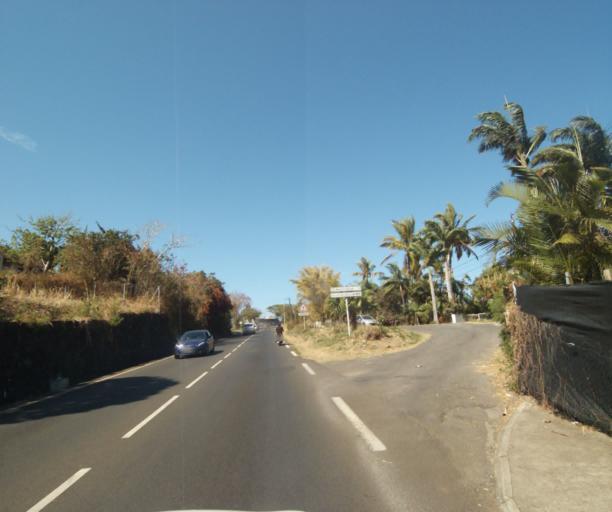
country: RE
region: Reunion
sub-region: Reunion
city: La Possession
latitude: -20.9879
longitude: 55.3315
